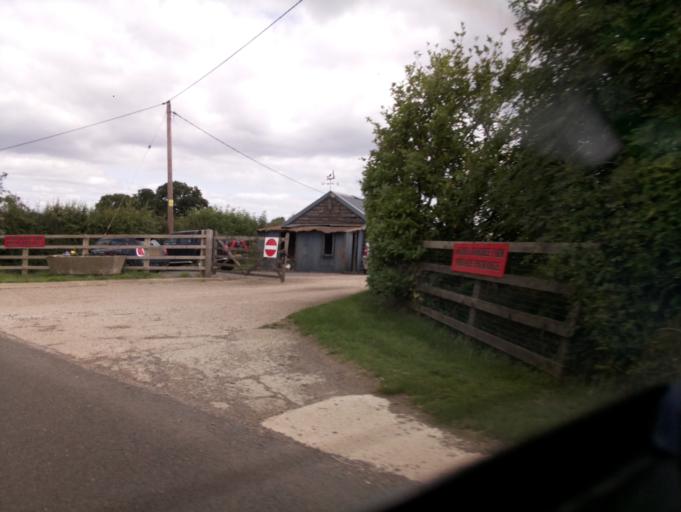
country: GB
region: England
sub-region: Buckinghamshire
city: Newton Longville
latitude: 51.9715
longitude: -0.8185
